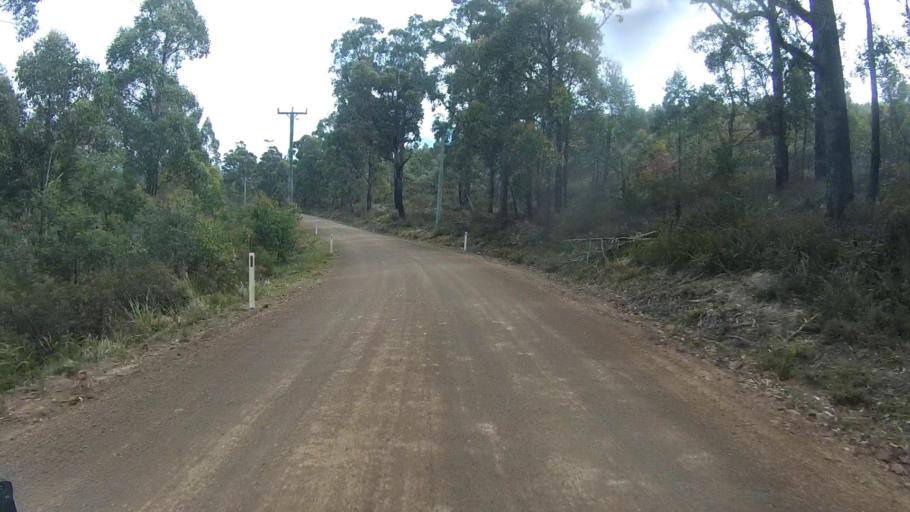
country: AU
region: Tasmania
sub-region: Sorell
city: Sorell
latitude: -42.7643
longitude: 147.8033
